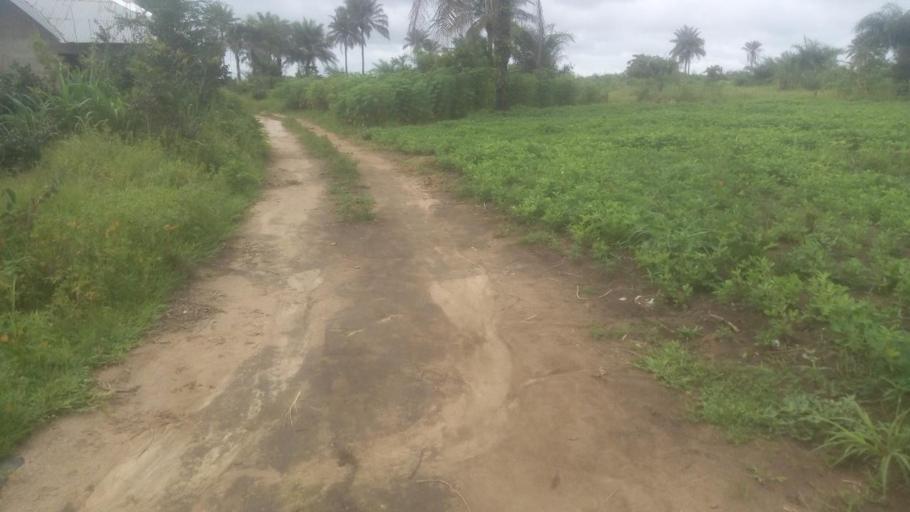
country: SL
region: Northern Province
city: Masoyila
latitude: 8.5904
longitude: -13.1848
